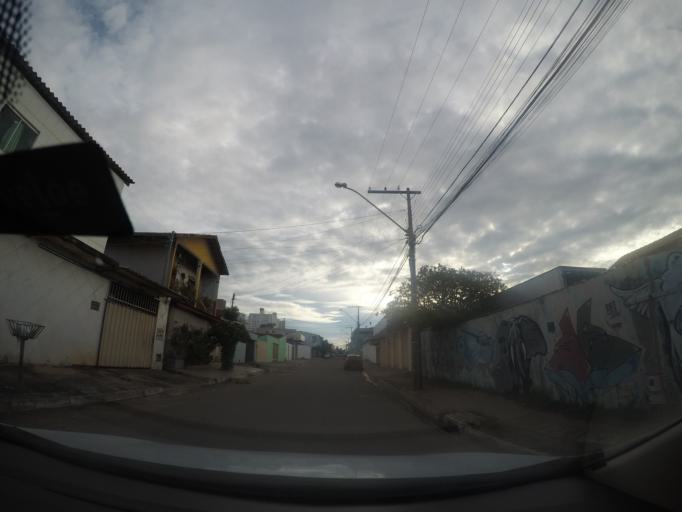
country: BR
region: Goias
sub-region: Goiania
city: Goiania
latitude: -16.6437
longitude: -49.3234
